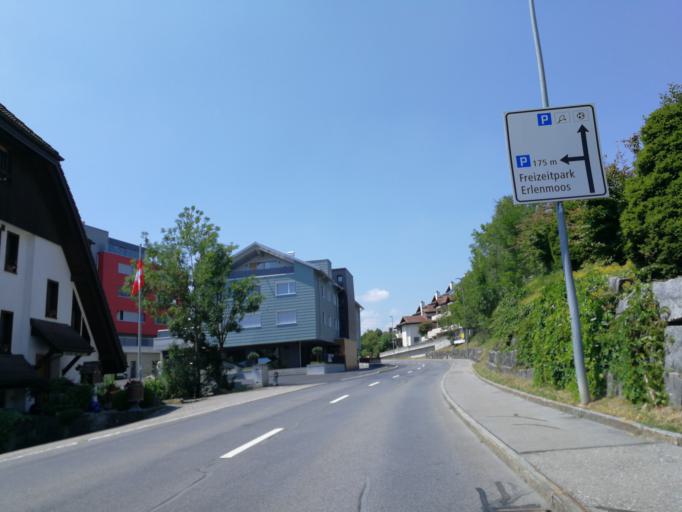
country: CH
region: Schwyz
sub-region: Bezirk Hoefe
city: Wollerau
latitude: 47.1901
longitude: 8.7069
